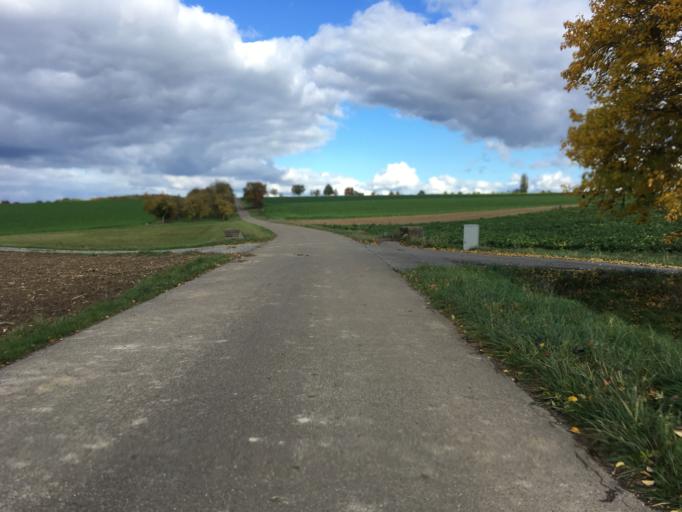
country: DE
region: Baden-Wuerttemberg
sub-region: Regierungsbezirk Stuttgart
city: Untermunkheim
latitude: 49.1819
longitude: 9.7073
